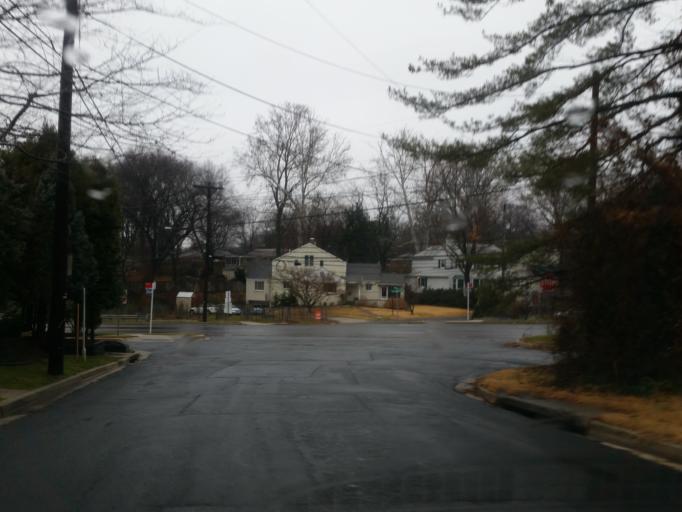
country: US
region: Maryland
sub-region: Montgomery County
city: Forest Glen
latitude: 38.9919
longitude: -77.0577
